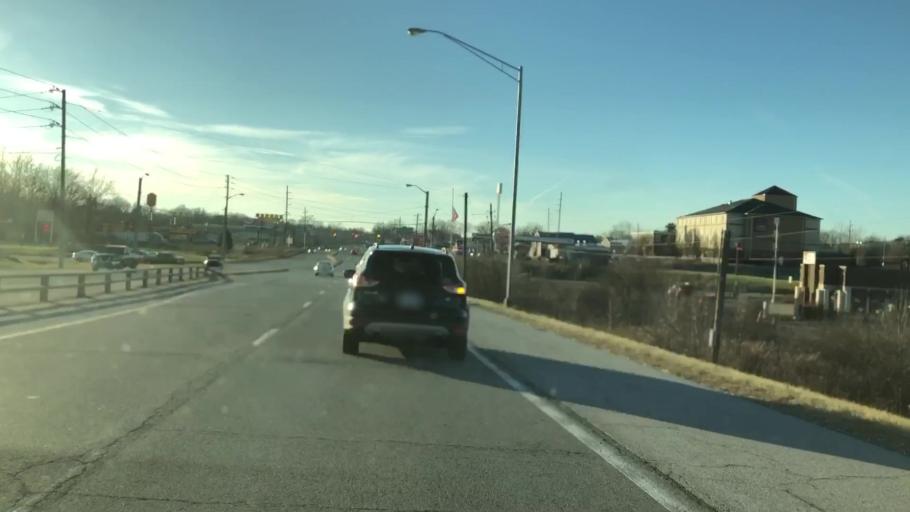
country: US
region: Indiana
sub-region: Marion County
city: Southport
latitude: 39.6657
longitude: -86.0936
